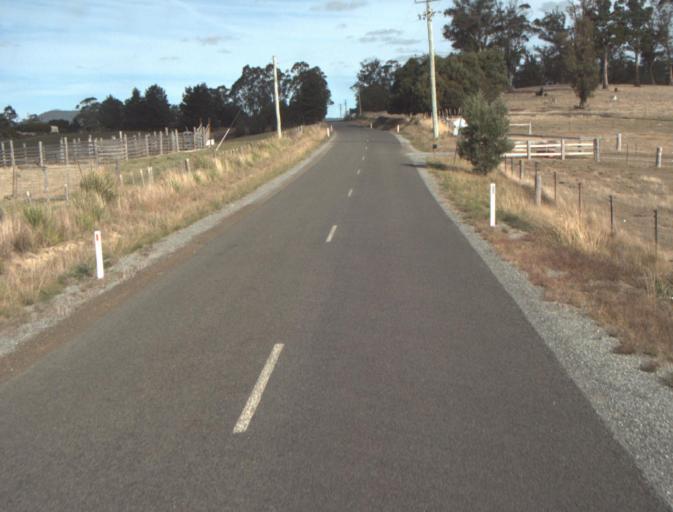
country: AU
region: Tasmania
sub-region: Launceston
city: Mayfield
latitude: -41.2129
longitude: 147.1344
